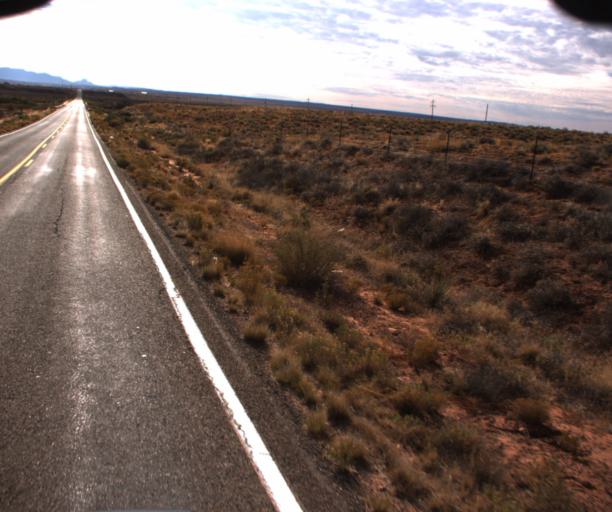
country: US
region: Arizona
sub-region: Apache County
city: Many Farms
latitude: 36.5324
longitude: -109.5099
